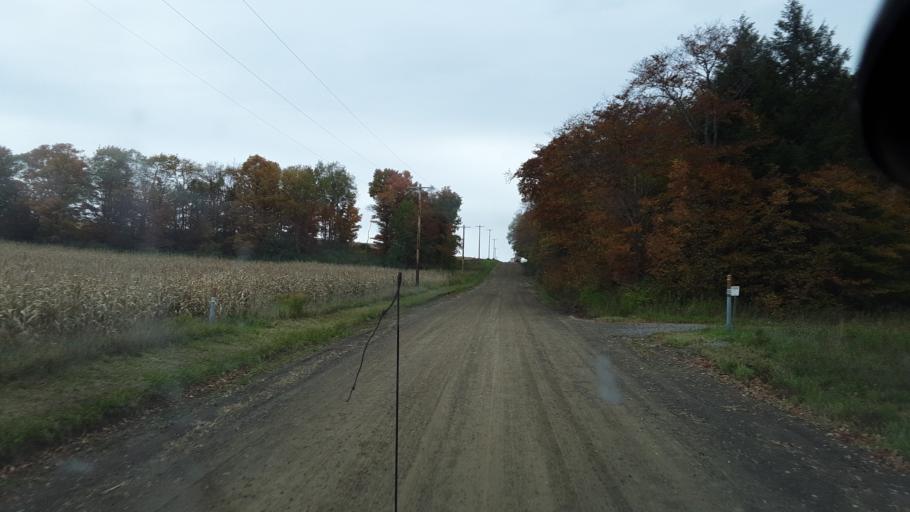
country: US
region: New York
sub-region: Allegany County
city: Andover
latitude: 42.0869
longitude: -77.7960
